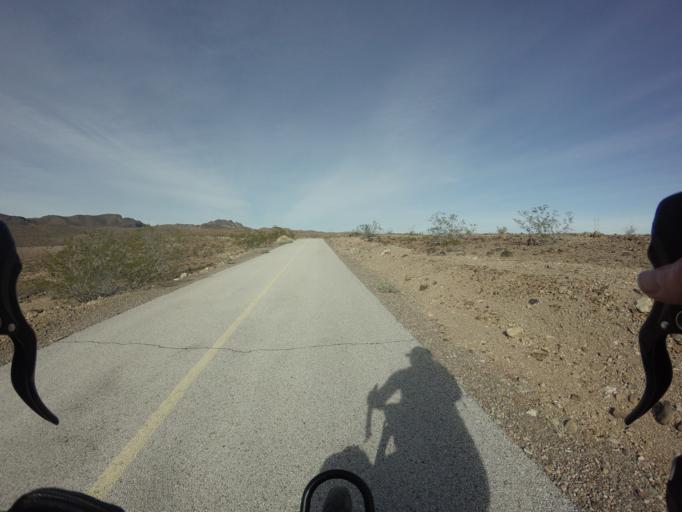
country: US
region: Nevada
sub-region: Clark County
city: Boulder City
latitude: 36.0770
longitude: -114.8195
